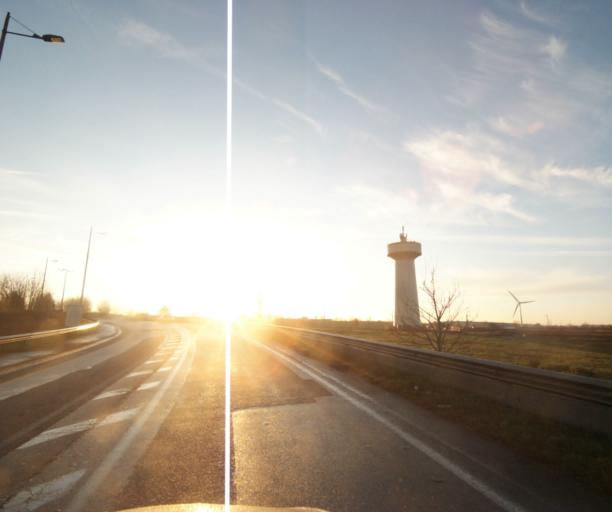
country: FR
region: Nord-Pas-de-Calais
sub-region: Departement du Nord
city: Onnaing
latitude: 50.3811
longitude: 3.6058
